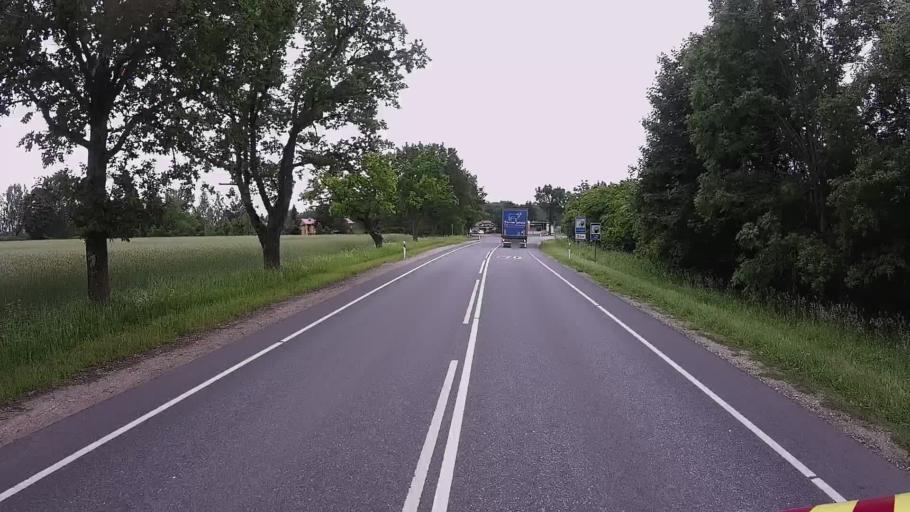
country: EE
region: Viljandimaa
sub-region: Karksi vald
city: Karksi-Nuia
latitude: 58.1212
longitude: 25.5826
